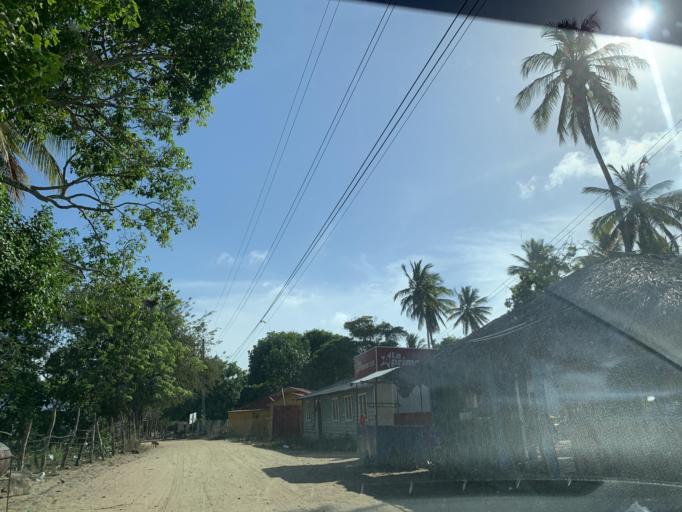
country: DO
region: Puerto Plata
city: Luperon
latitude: 19.8996
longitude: -70.8789
